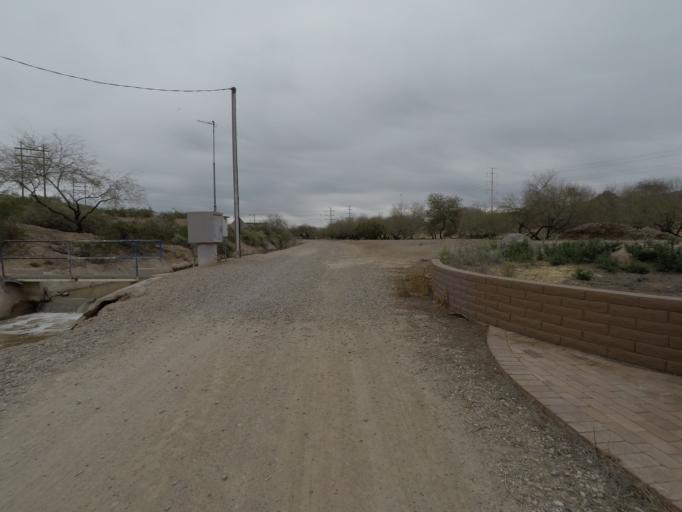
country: US
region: Arizona
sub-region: Maricopa County
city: Tempe Junction
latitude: 33.4363
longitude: -111.9398
